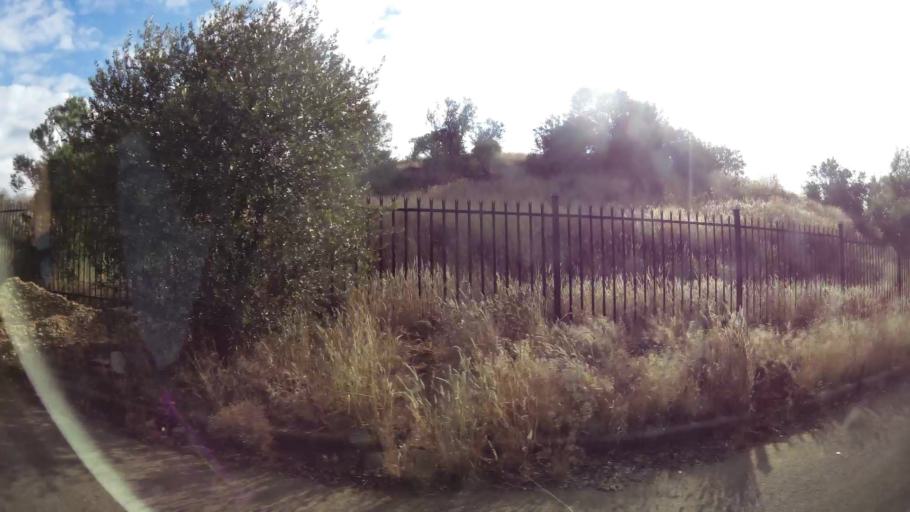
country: ZA
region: Orange Free State
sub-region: Mangaung Metropolitan Municipality
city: Bloemfontein
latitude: -29.0783
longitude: 26.2398
